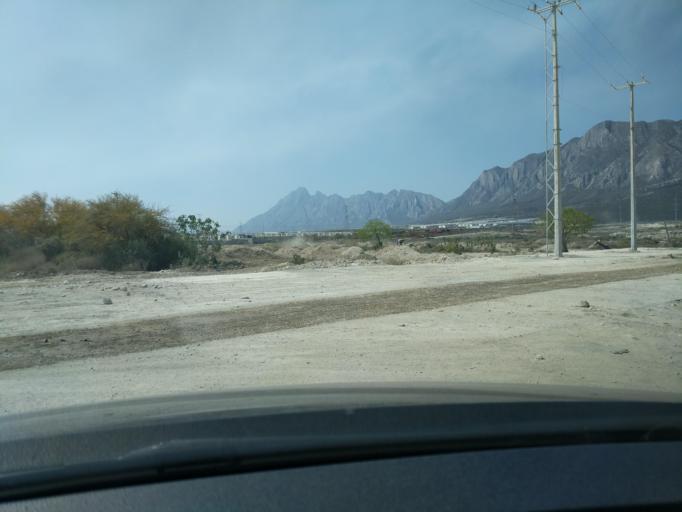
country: MX
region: Nuevo Leon
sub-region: Garcia
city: Valle de Lincoln
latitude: 25.7977
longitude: -100.4717
